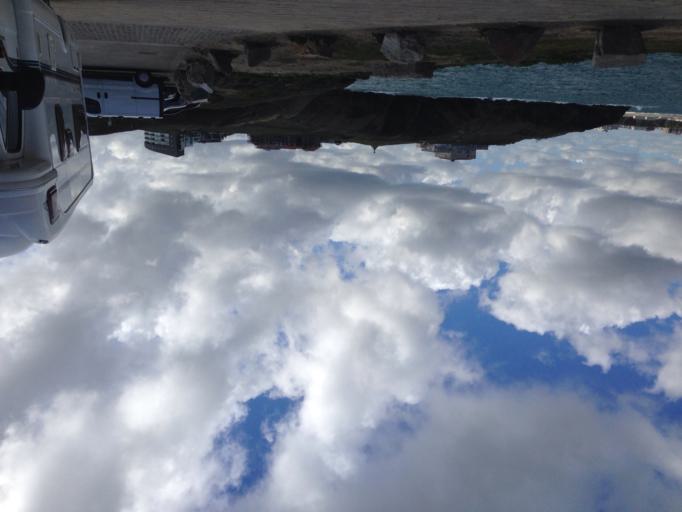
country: GB
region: England
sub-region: Cornwall
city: Newquay
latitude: 50.4235
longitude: -5.0975
